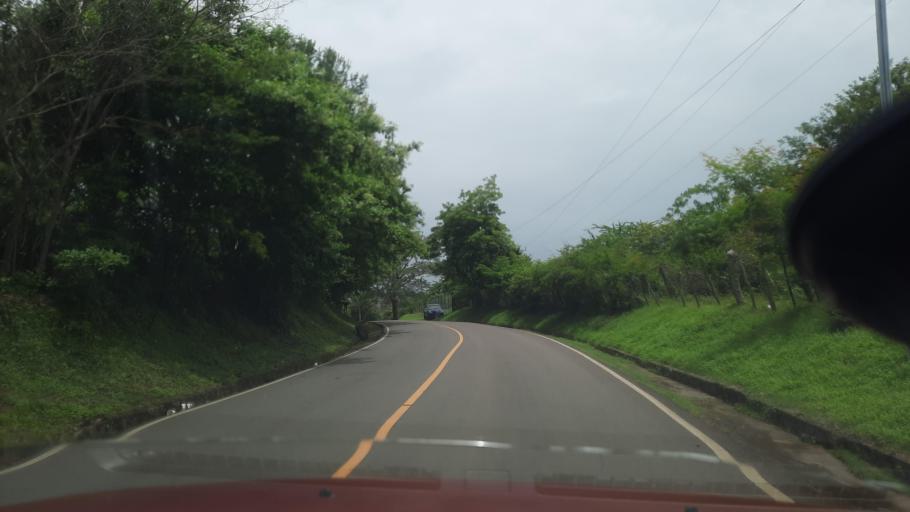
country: SV
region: La Union
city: Santa Rosa de Lima
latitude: 13.6456
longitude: -87.8577
